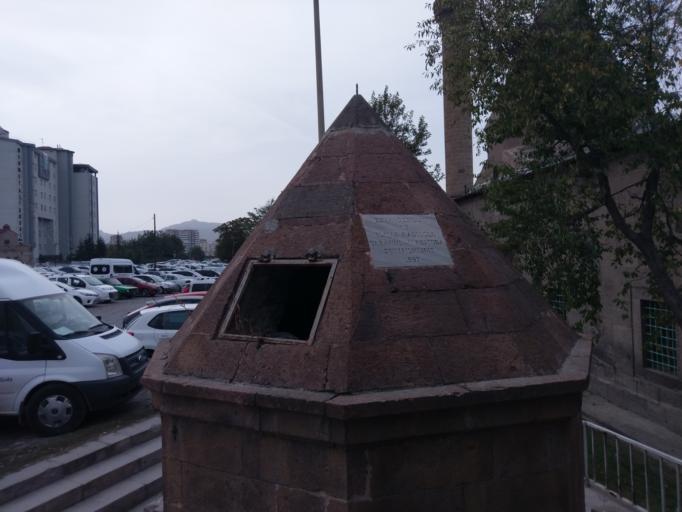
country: TR
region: Kayseri
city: Kayseri
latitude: 38.7158
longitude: 35.4902
